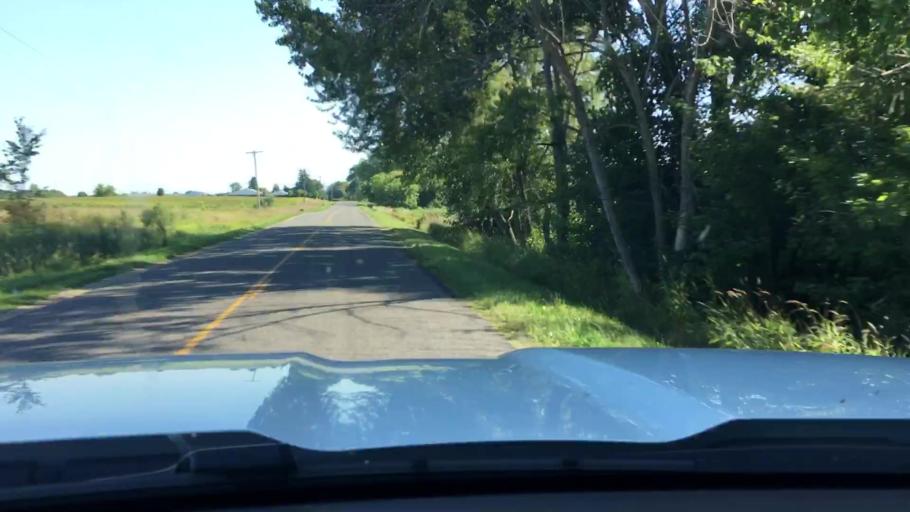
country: US
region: Michigan
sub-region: Muskegon County
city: Ravenna
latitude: 43.2407
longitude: -85.9180
